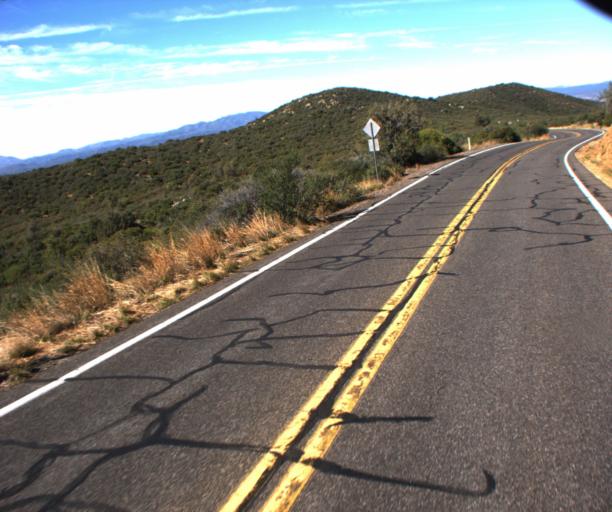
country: US
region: Arizona
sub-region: Yavapai County
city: Prescott
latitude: 34.4256
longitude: -112.5546
